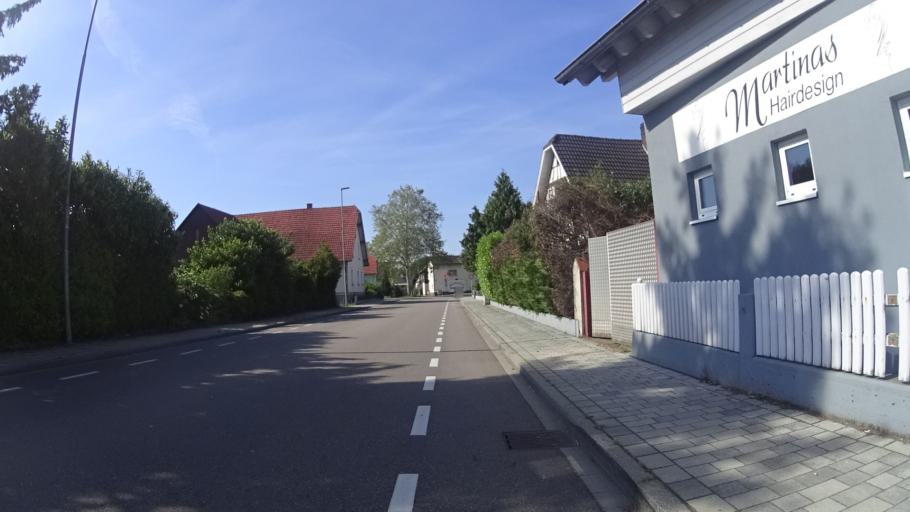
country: DE
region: Baden-Wuerttemberg
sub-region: Freiburg Region
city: Kehl
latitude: 48.5240
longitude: 7.8251
